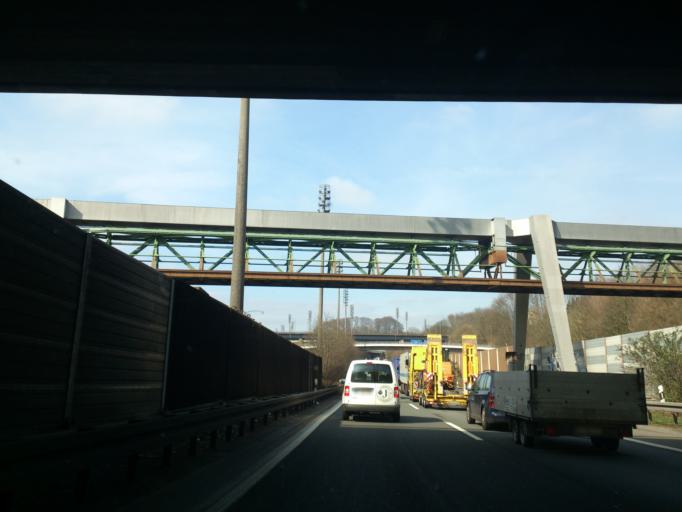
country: DE
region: North Rhine-Westphalia
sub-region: Regierungsbezirk Dusseldorf
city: Solingen
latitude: 51.2374
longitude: 7.0932
